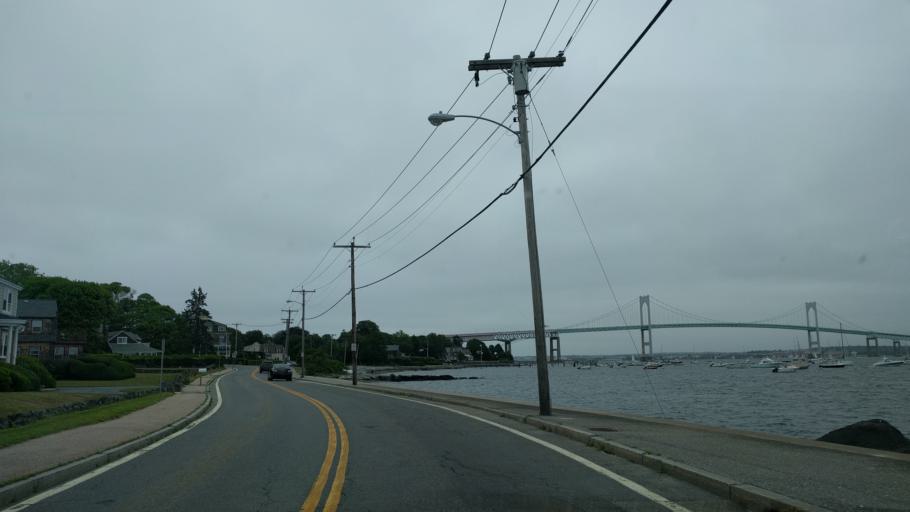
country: US
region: Rhode Island
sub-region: Newport County
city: Jamestown
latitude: 41.4996
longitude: -71.3655
